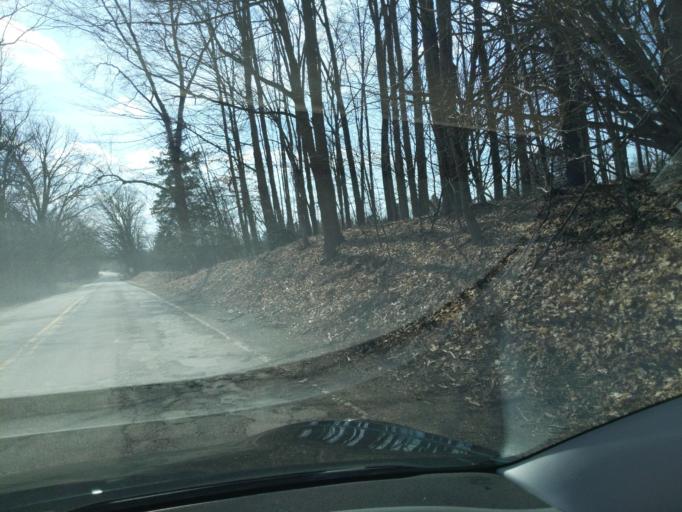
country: US
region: Michigan
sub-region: Livingston County
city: Pinckney
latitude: 42.4412
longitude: -84.0602
